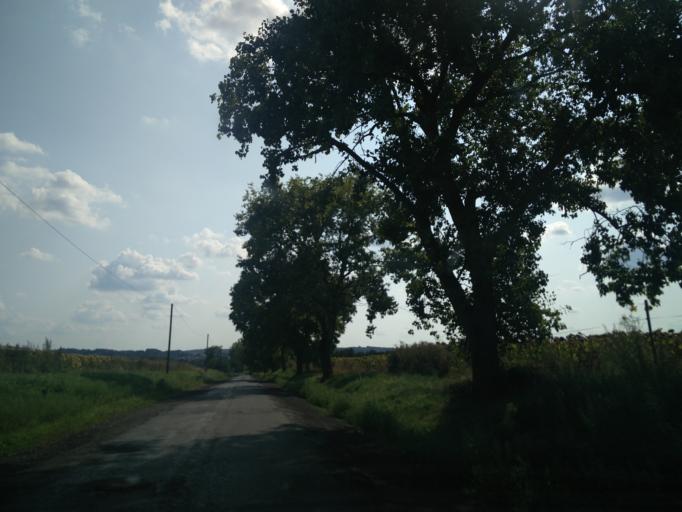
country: HU
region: Zala
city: Zalaegerszeg
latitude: 46.8887
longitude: 16.7567
